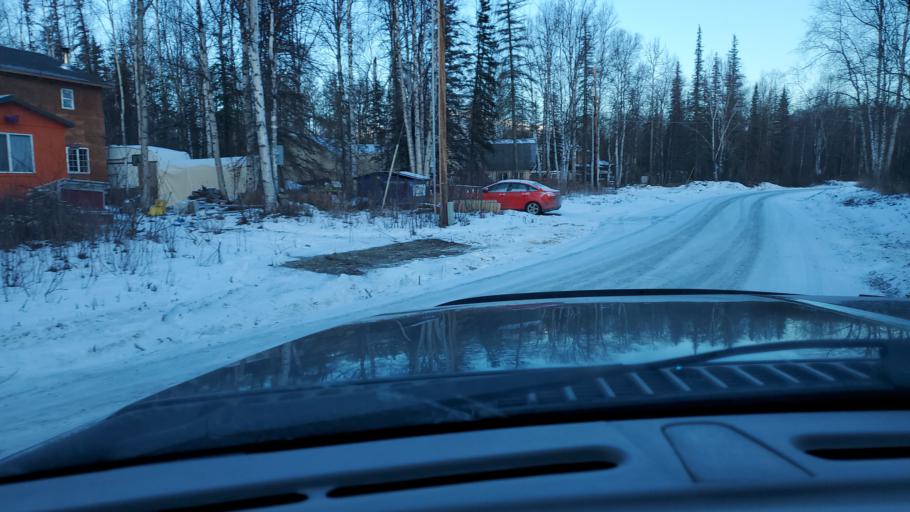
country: US
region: Alaska
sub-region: Matanuska-Susitna Borough
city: Lakes
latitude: 61.6649
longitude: -149.2998
